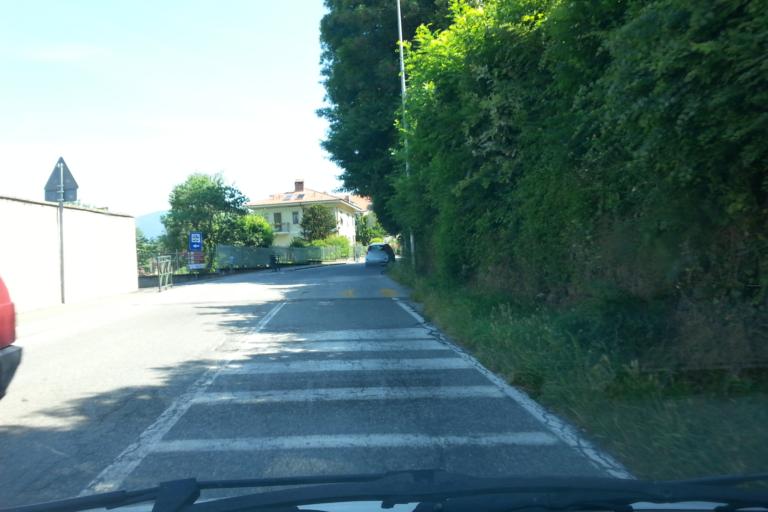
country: IT
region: Piedmont
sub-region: Provincia di Torino
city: Avigliana
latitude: 45.0708
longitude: 7.3922
